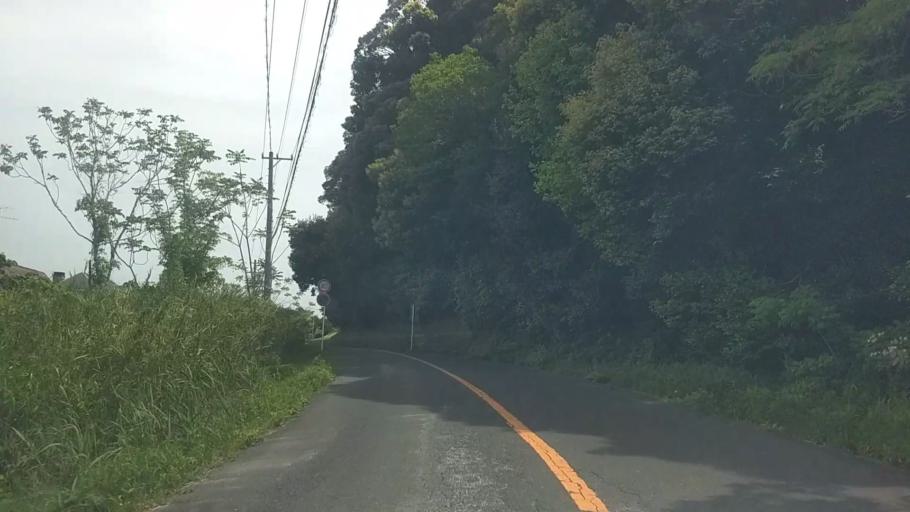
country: JP
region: Shizuoka
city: Kosai-shi
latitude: 34.7535
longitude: 137.5155
